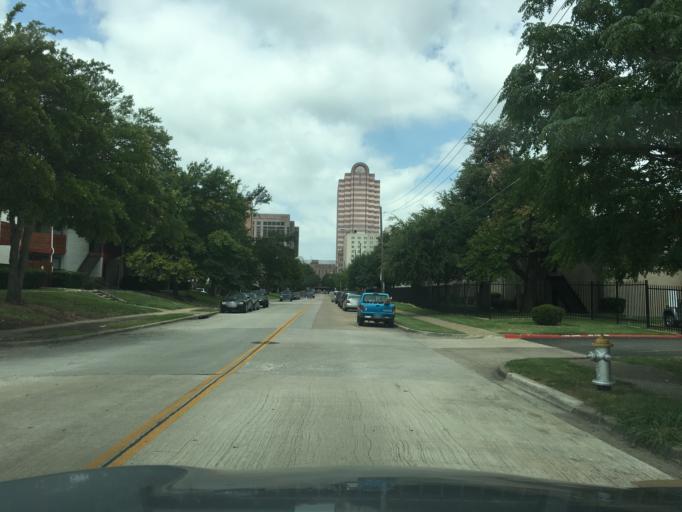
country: US
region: Texas
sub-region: Dallas County
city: Addison
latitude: 32.9306
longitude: -96.8135
